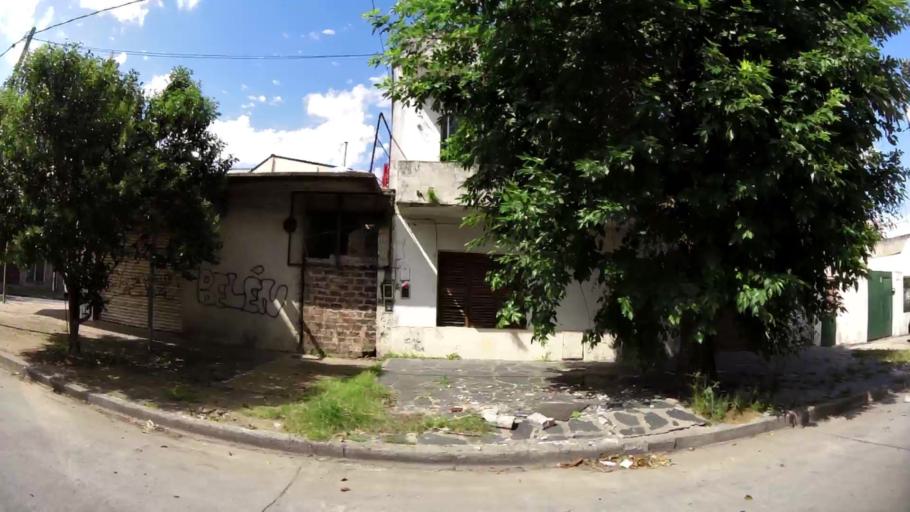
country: AR
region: Buenos Aires
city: San Justo
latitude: -34.6559
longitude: -58.5365
